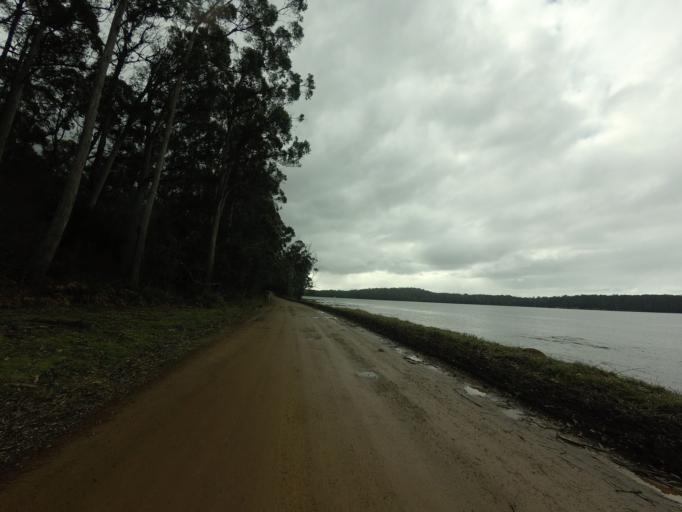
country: AU
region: Tasmania
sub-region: Huon Valley
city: Geeveston
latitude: -43.5326
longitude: 146.8928
